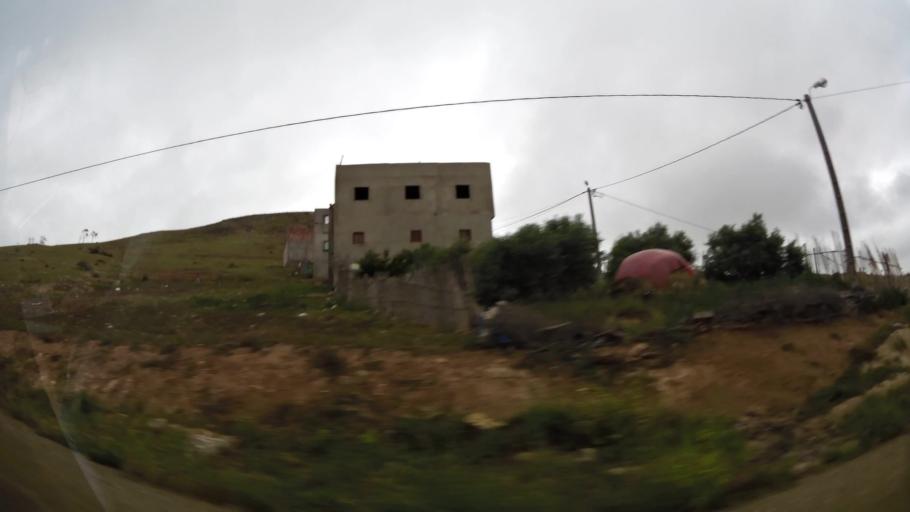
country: MA
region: Oriental
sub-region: Nador
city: Midar
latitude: 35.0648
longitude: -3.4704
